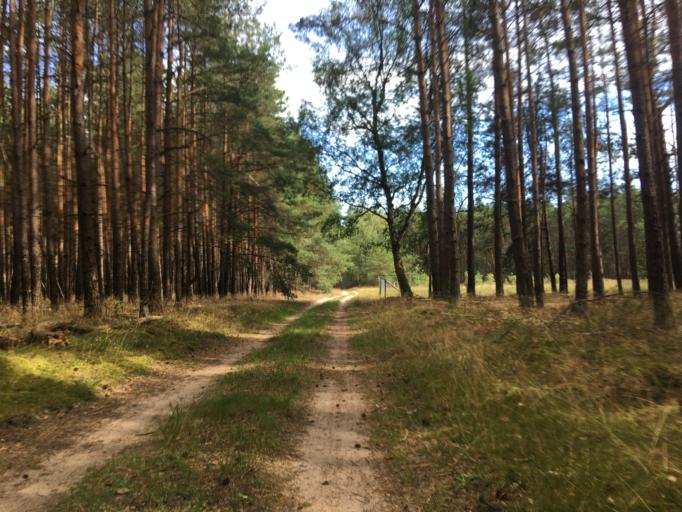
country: DE
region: Brandenburg
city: Rheinsberg
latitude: 53.0352
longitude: 12.9226
